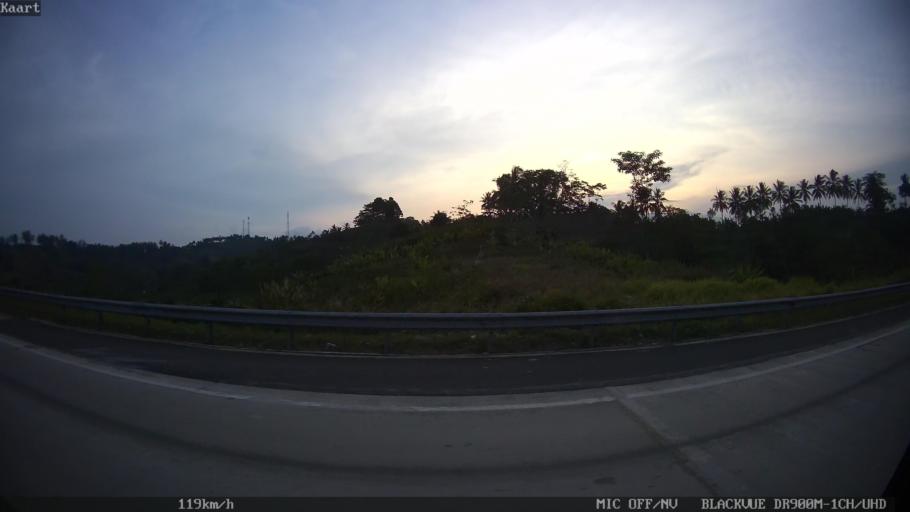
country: ID
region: Lampung
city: Penengahan
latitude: -5.7995
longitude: 105.7294
